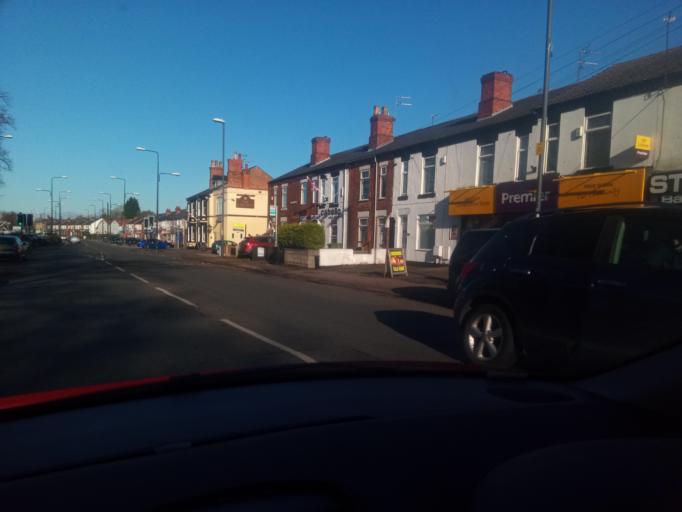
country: GB
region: England
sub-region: Derby
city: Derby
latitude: 52.8887
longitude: -1.4509
